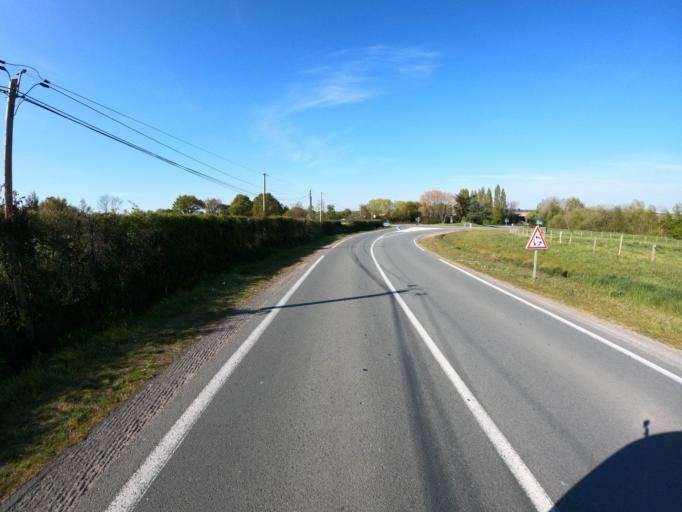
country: FR
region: Pays de la Loire
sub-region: Departement de la Vendee
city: Mortagne-sur-Sevre
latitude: 47.0015
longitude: -0.9417
